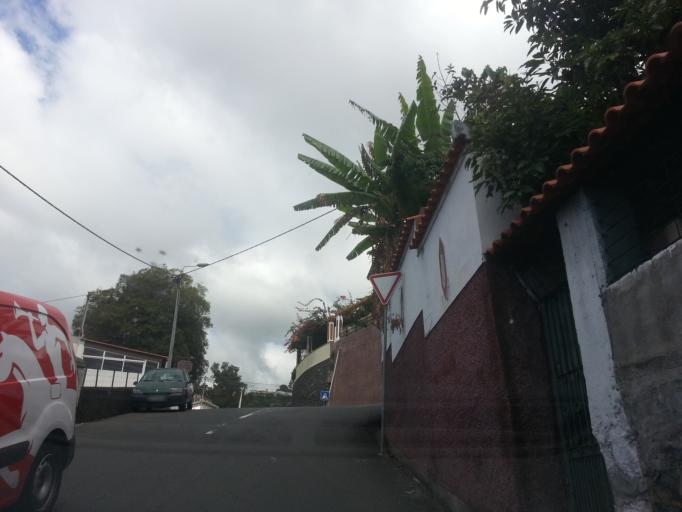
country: PT
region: Madeira
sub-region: Funchal
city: Nossa Senhora do Monte
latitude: 32.6715
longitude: -16.9389
